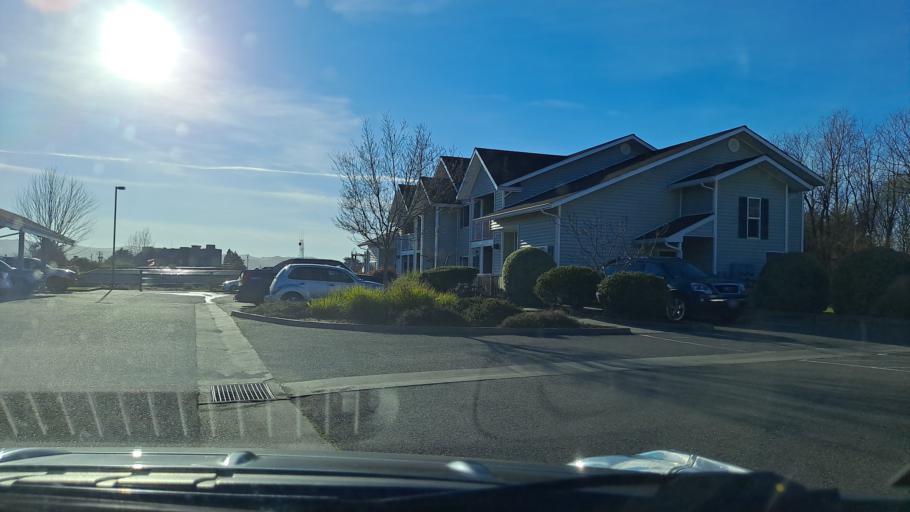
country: US
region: California
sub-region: Humboldt County
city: Fortuna
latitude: 40.5937
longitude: -124.1439
